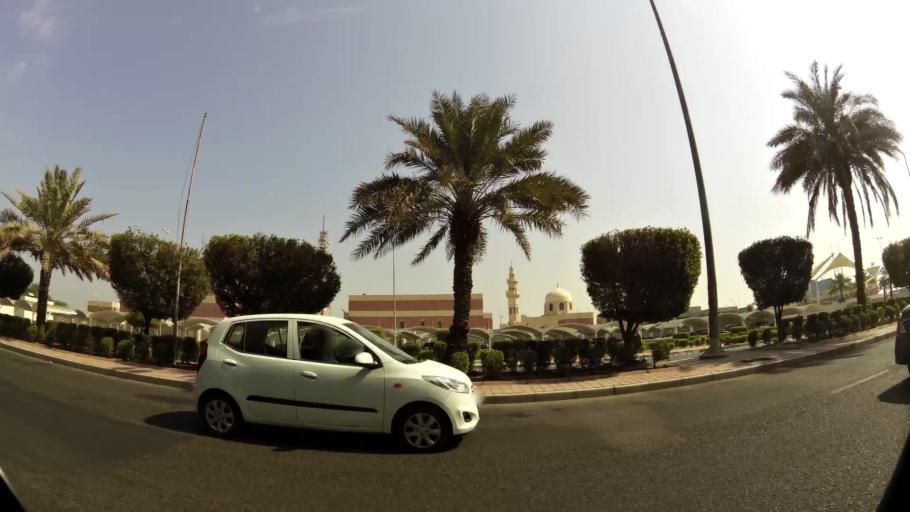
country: KW
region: Al Ahmadi
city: Al Fintas
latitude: 29.1682
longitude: 48.1229
